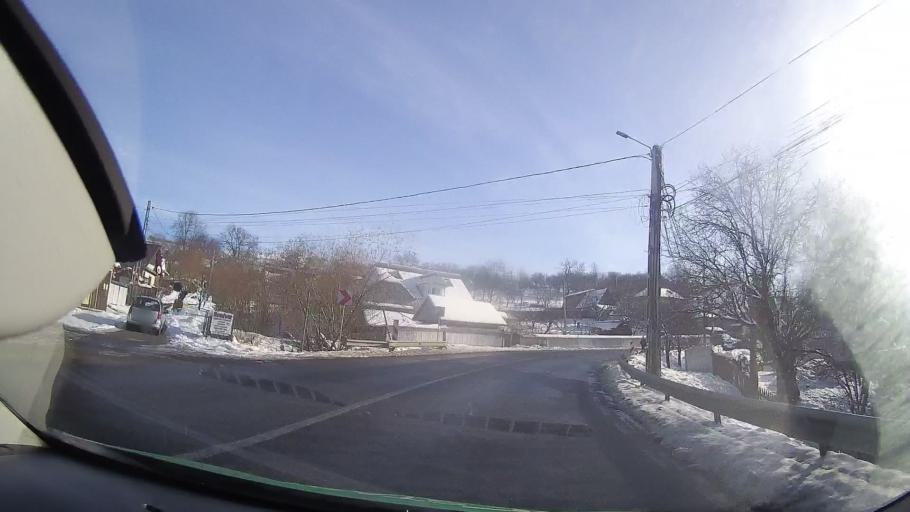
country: RO
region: Neamt
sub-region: Comuna Baltatesti
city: Baltatesti
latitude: 47.1183
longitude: 26.3122
